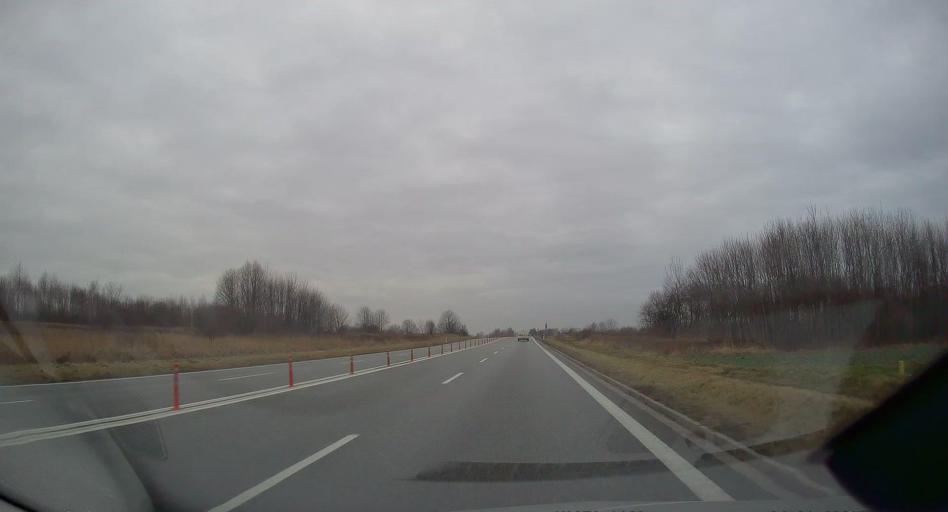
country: PL
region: Subcarpathian Voivodeship
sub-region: Powiat rzeszowski
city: Trzciana
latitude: 50.0717
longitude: 21.8573
